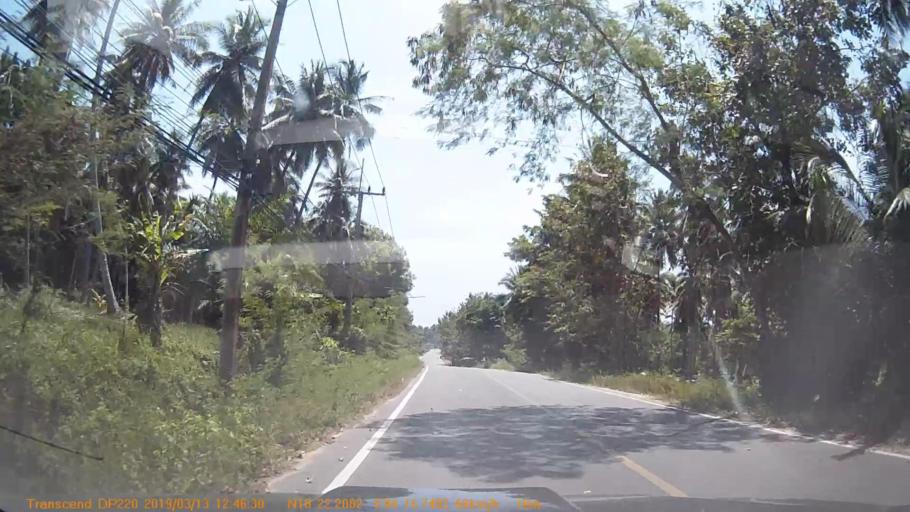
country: TH
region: Chumphon
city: Chumphon
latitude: 10.3696
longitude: 99.2624
